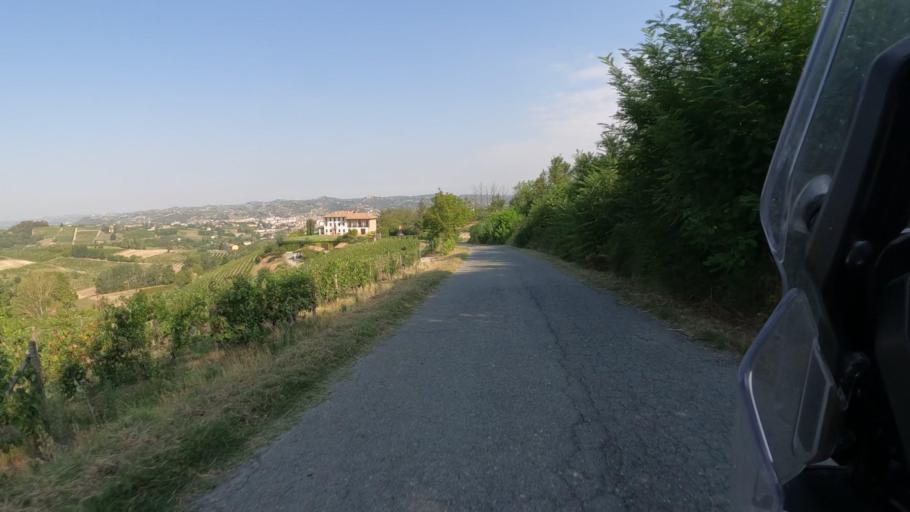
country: IT
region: Piedmont
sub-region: Provincia di Asti
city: Nizza Monferrato
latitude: 44.7569
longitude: 8.3823
